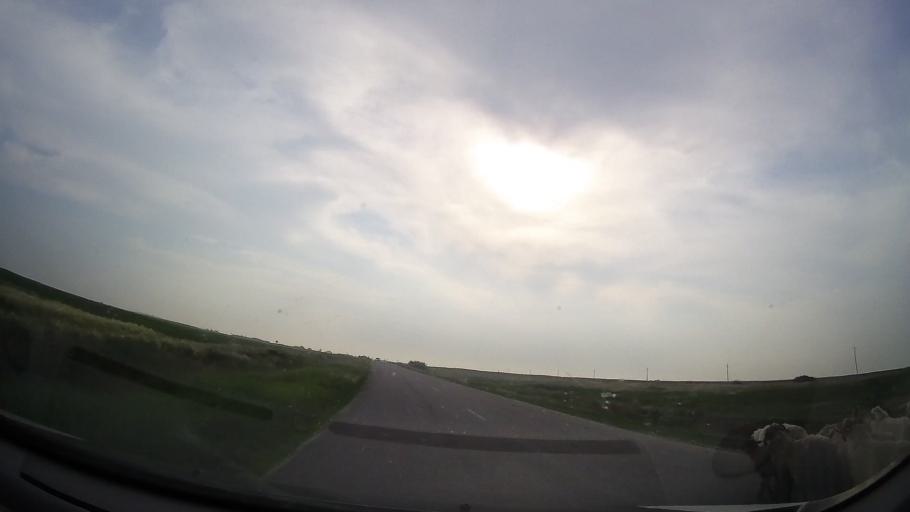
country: RO
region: Timis
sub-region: Comuna Foeni
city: Foeni
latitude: 45.4913
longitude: 20.8443
